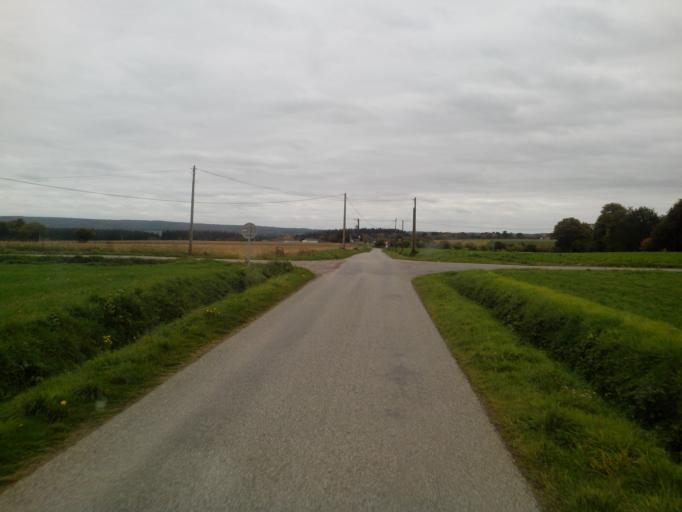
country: FR
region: Brittany
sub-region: Departement du Morbihan
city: Mauron
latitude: 48.0765
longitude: -2.3142
